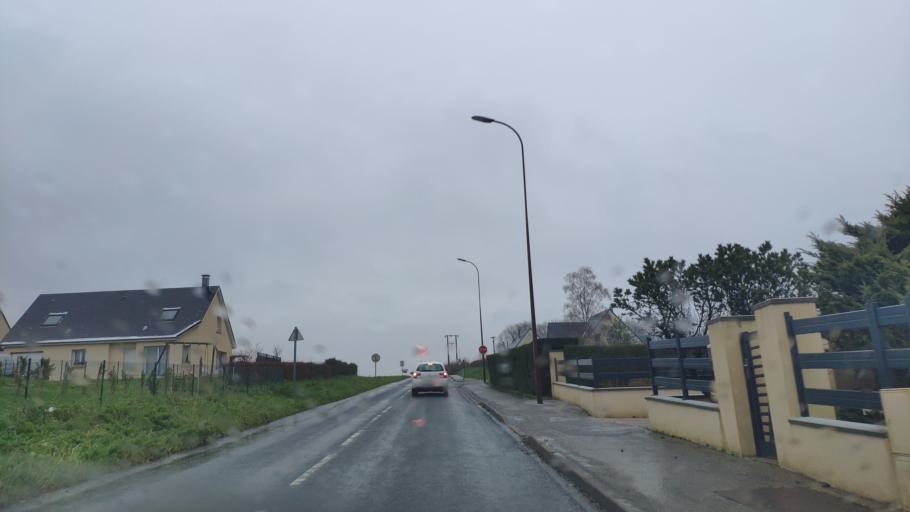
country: FR
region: Haute-Normandie
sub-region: Departement de la Seine-Maritime
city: Cany-Barville
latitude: 49.7890
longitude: 0.6466
